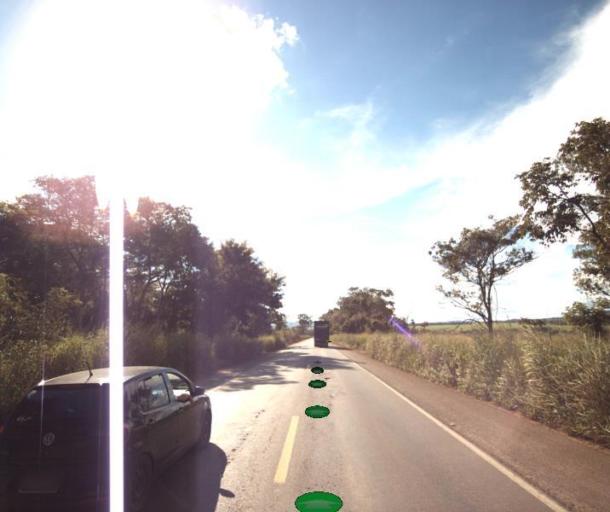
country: BR
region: Goias
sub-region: Rialma
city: Rialma
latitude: -15.4076
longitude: -49.5302
